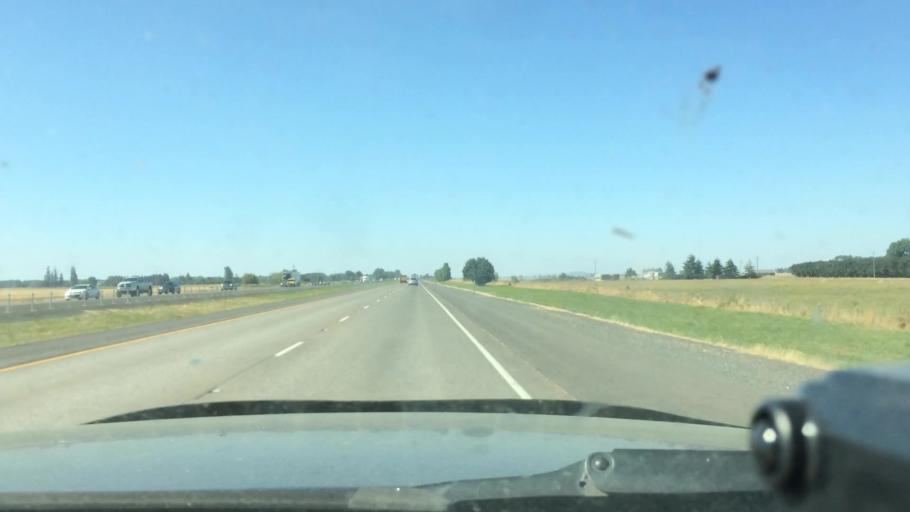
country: US
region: Oregon
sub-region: Linn County
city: Tangent
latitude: 44.4789
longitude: -123.0614
